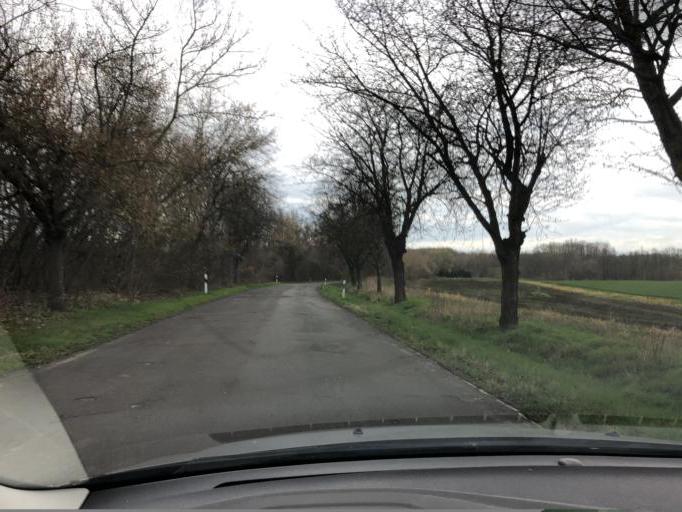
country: DE
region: Saxony-Anhalt
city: Muschwitz
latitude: 51.1786
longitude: 12.1327
